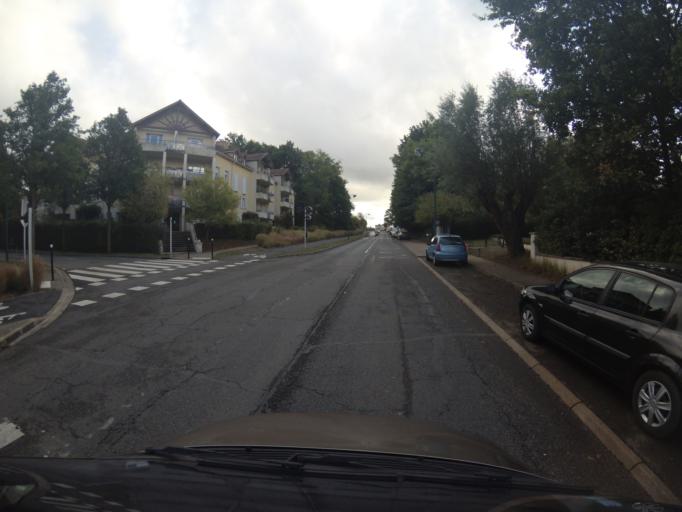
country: FR
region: Ile-de-France
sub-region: Departement de Seine-et-Marne
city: Montevrain
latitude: 48.8688
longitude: 2.7528
